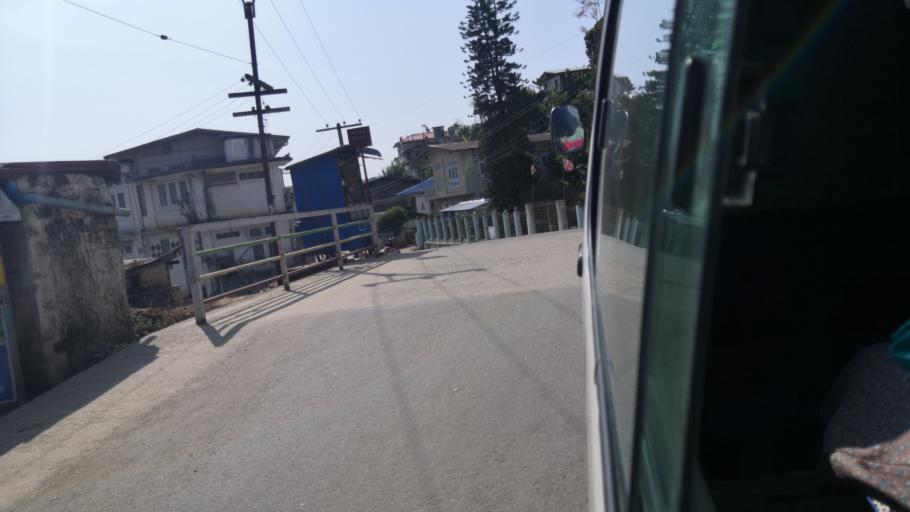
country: MM
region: Mandalay
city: Mogok
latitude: 22.9267
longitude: 96.5050
